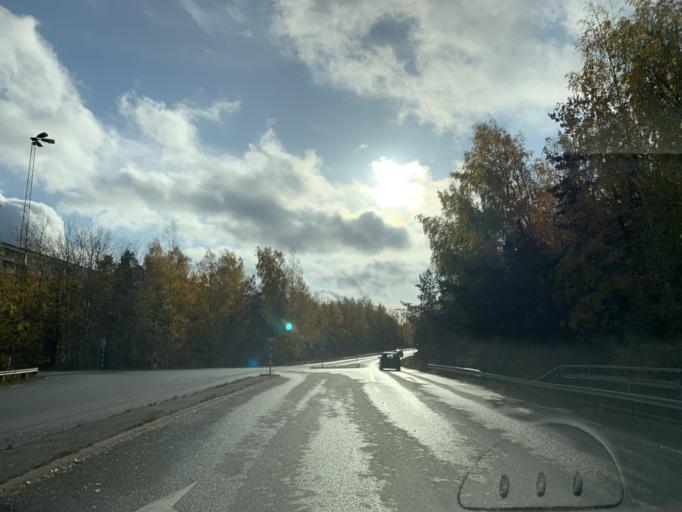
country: SE
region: Stockholm
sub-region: Haninge Kommun
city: Haninge
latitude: 59.1736
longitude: 18.1615
